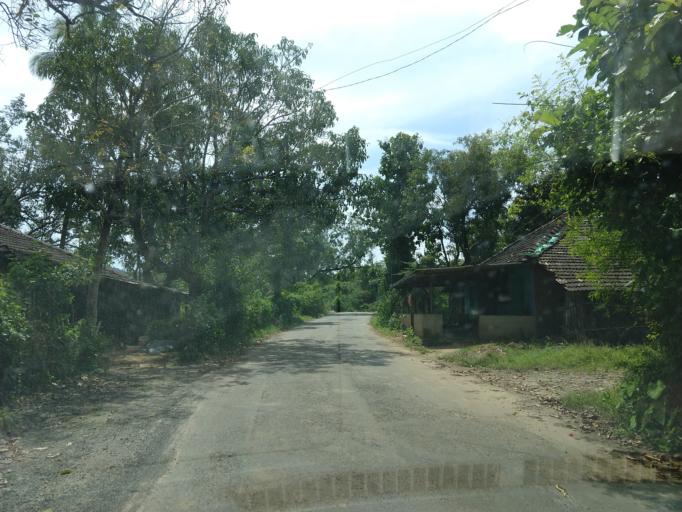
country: IN
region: Maharashtra
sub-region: Sindhudurg
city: Savantvadi
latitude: 15.9595
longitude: 73.7724
